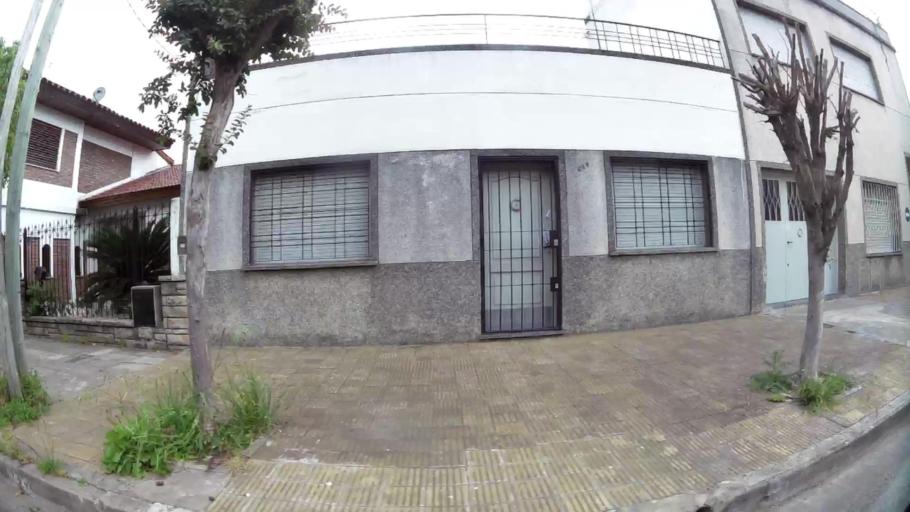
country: AR
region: Buenos Aires
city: San Justo
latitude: -34.6633
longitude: -58.5277
